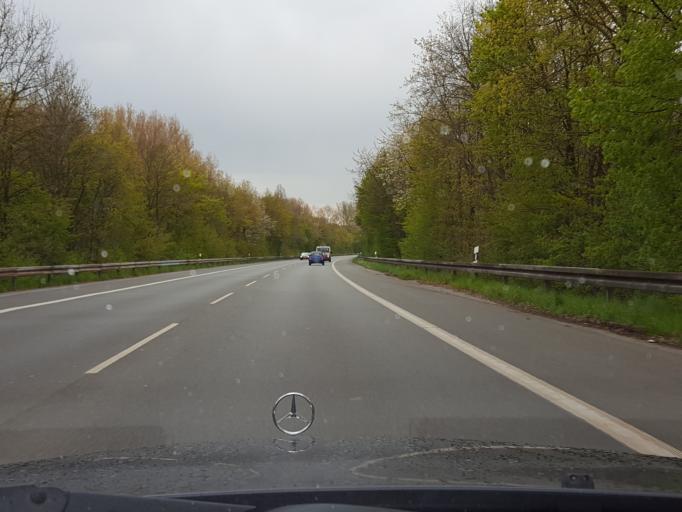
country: DE
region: North Rhine-Westphalia
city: Datteln
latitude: 51.6531
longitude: 7.3615
